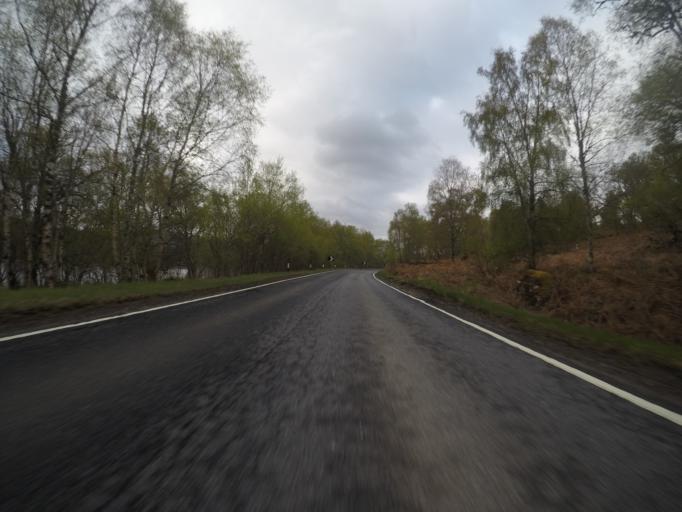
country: GB
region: Scotland
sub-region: Highland
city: Kingussie
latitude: 56.9673
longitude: -4.4409
